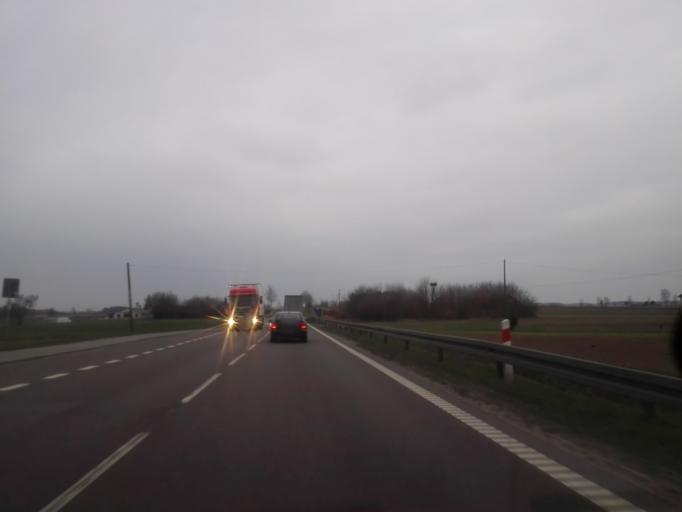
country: PL
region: Podlasie
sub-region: Powiat grajewski
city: Szczuczyn
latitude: 53.5880
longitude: 22.3308
